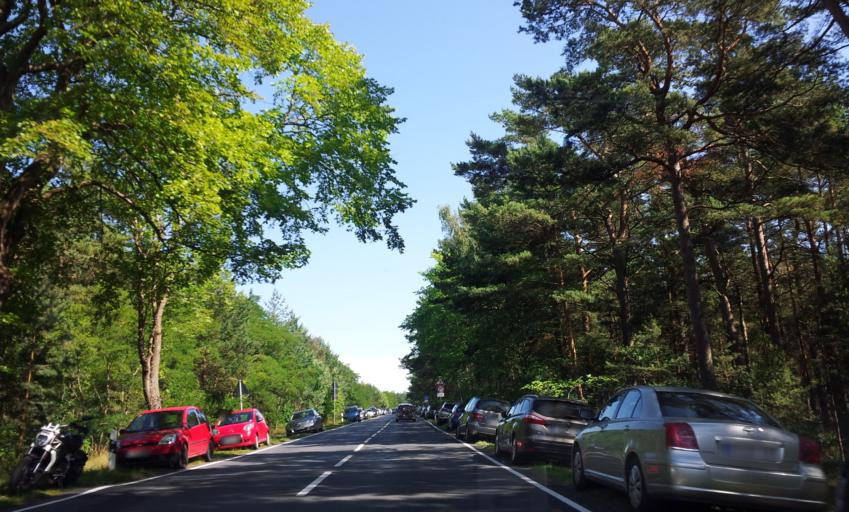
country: DE
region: Mecklenburg-Vorpommern
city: Glowe
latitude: 54.5734
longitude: 13.4260
